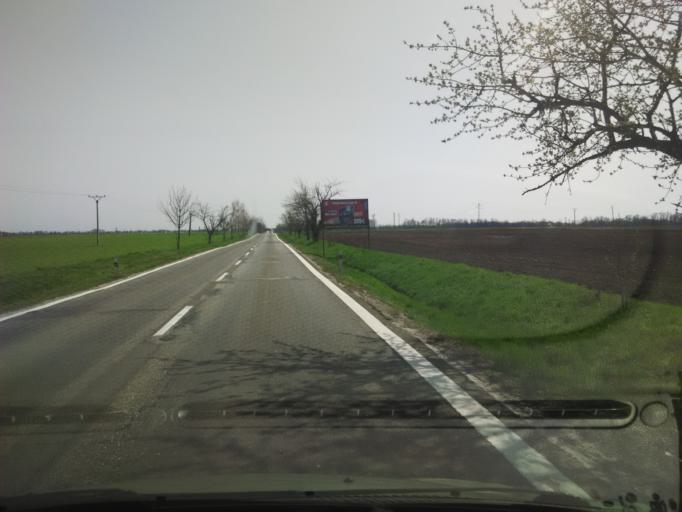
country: SK
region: Nitriansky
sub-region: Okres Nove Zamky
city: Nove Zamky
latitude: 48.0312
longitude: 18.1320
